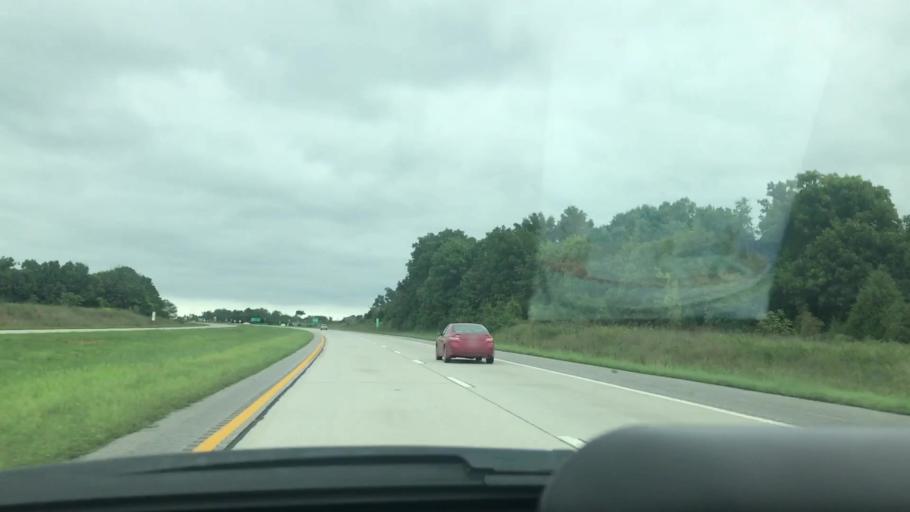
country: US
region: Missouri
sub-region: Greene County
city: Fair Grove
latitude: 37.4527
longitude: -93.1405
